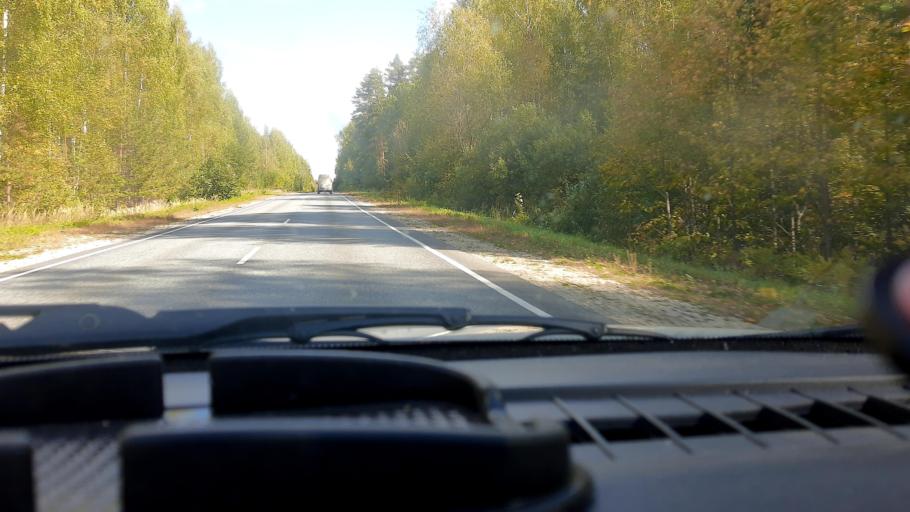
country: RU
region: Kirov
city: Sanchursk
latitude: 56.5748
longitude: 47.1857
